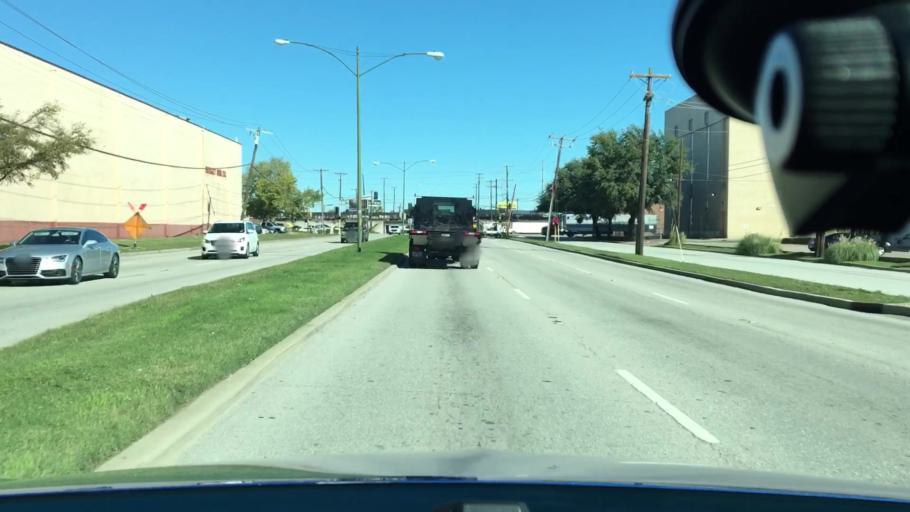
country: US
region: Texas
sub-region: Dallas County
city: Dallas
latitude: 32.8105
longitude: -96.8736
